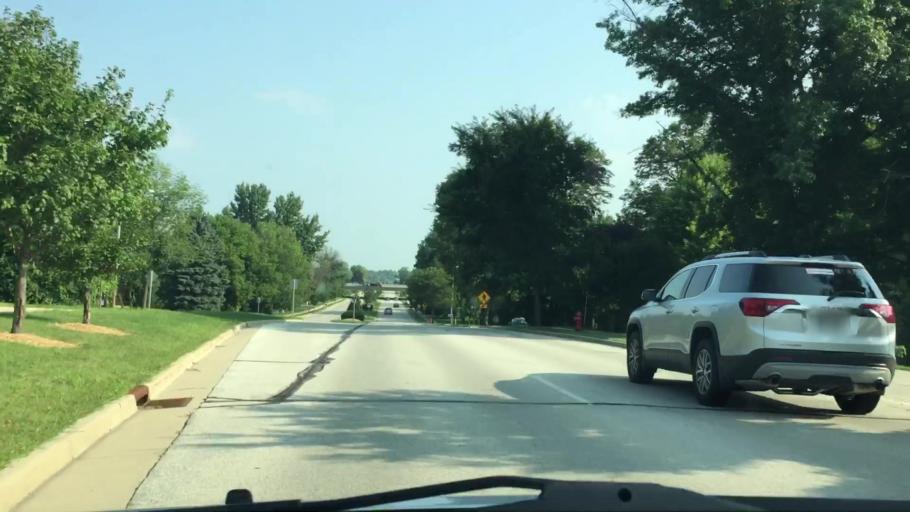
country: US
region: Wisconsin
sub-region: Waukesha County
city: Brookfield
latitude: 43.0236
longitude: -88.1269
